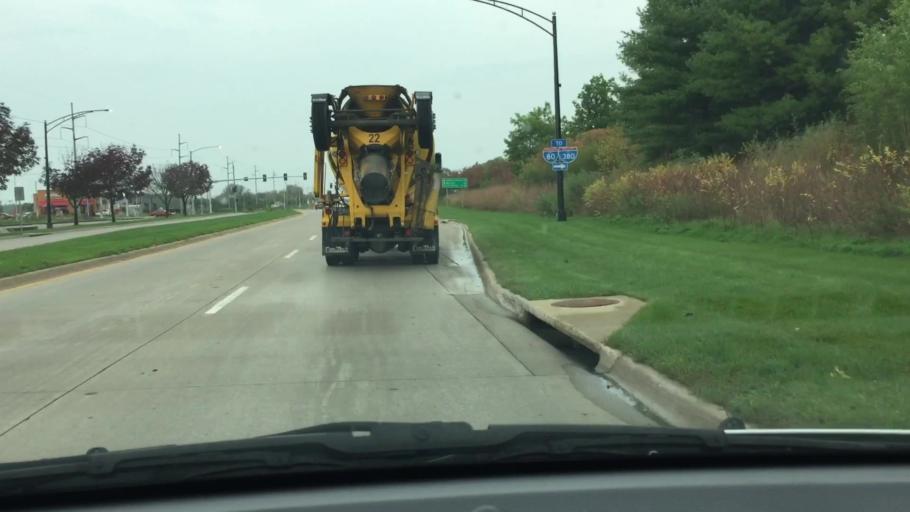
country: US
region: Iowa
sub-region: Johnson County
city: Coralville
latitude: 41.6876
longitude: -91.6069
